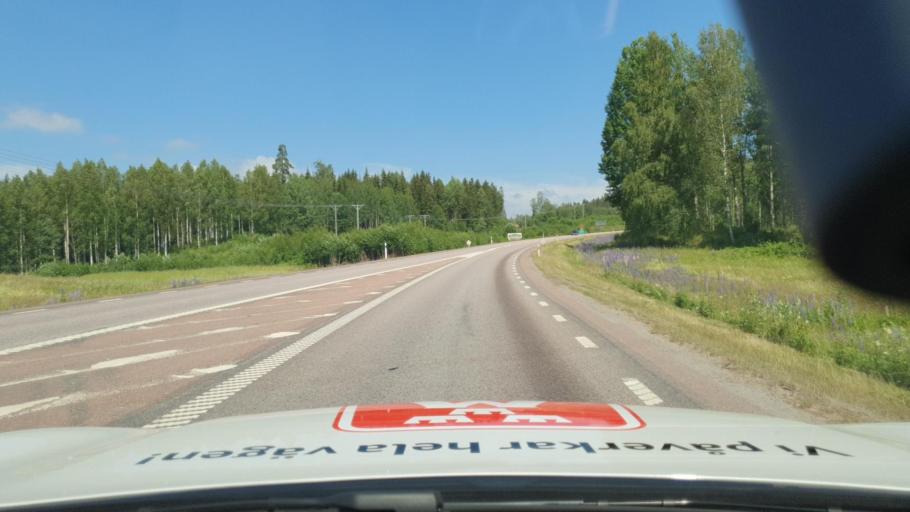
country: SE
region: Vaermland
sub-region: Torsby Kommun
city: Torsby
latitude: 60.1381
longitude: 12.9877
